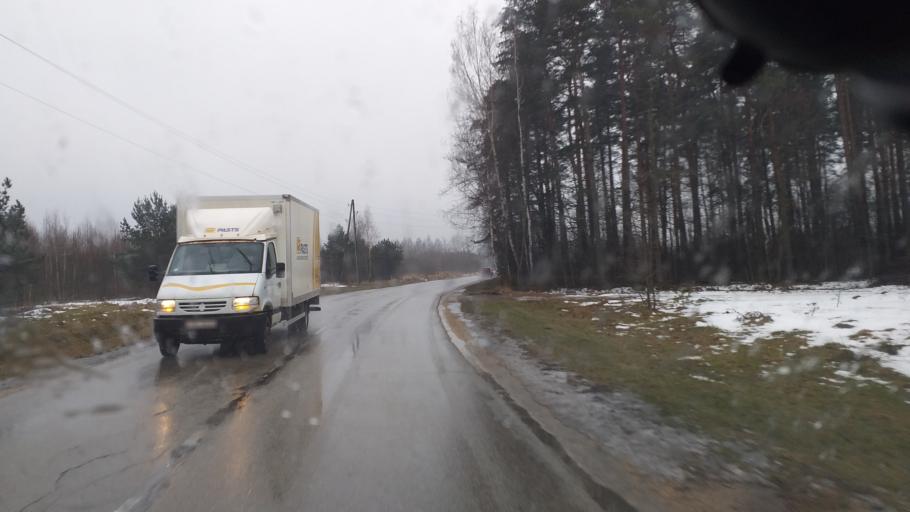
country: LV
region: Babite
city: Pinki
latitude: 56.9716
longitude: 23.9695
